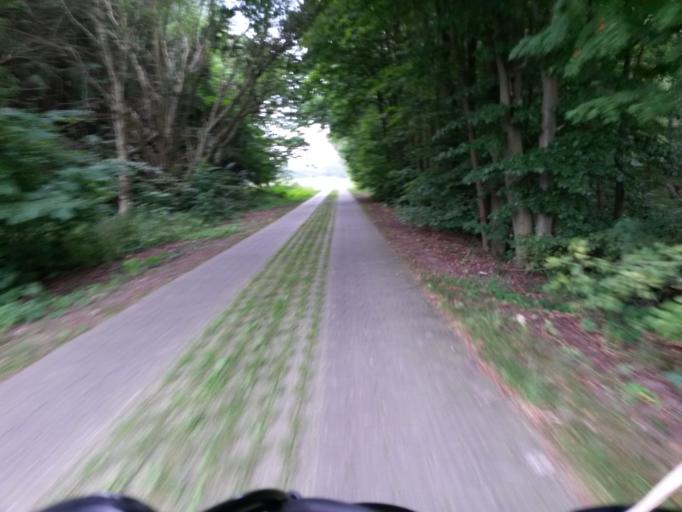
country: DE
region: Brandenburg
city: Angermunde
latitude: 53.0439
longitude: 13.9425
